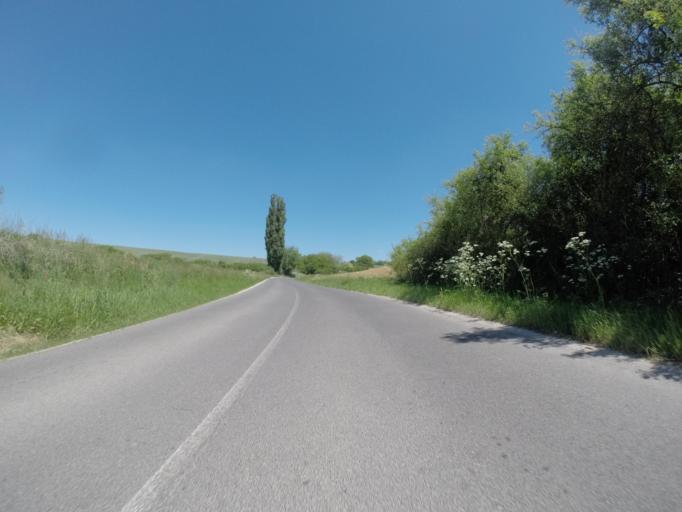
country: SK
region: Trnavsky
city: Hlohovec
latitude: 48.4602
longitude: 17.8447
